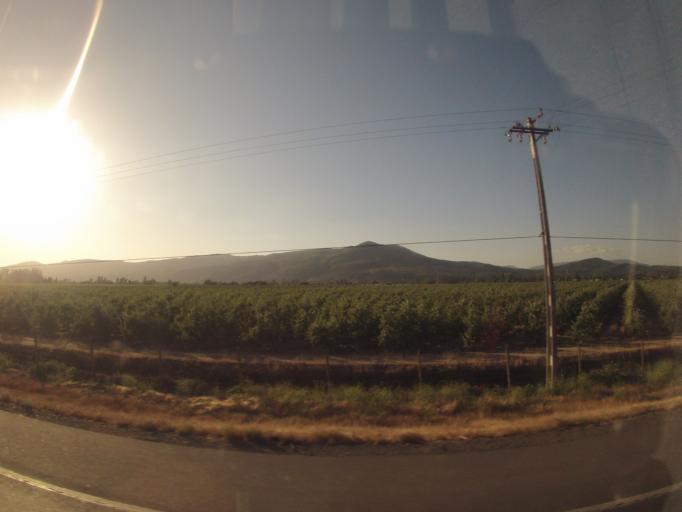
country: CL
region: O'Higgins
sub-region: Provincia de Colchagua
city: Chimbarongo
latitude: -34.7010
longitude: -71.0228
